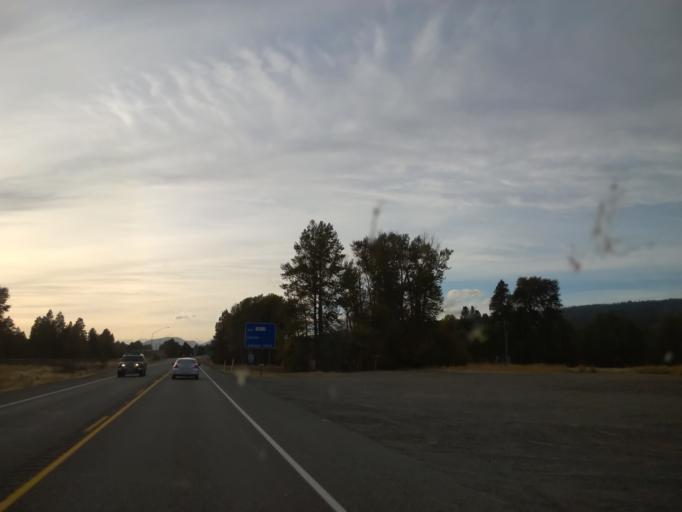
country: US
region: Washington
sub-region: Kittitas County
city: Cle Elum
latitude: 47.1852
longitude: -120.8925
